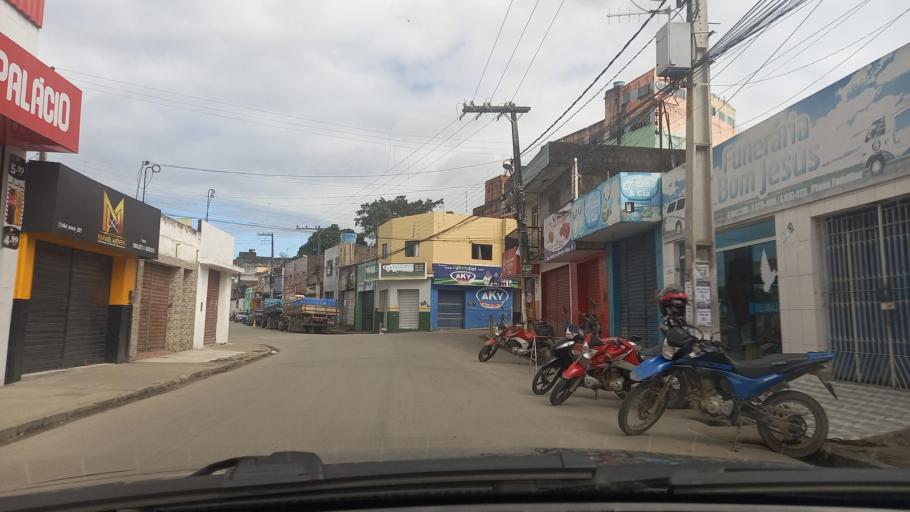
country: BR
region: Pernambuco
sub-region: Vitoria De Santo Antao
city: Vitoria de Santo Antao
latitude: -8.1192
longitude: -35.2926
